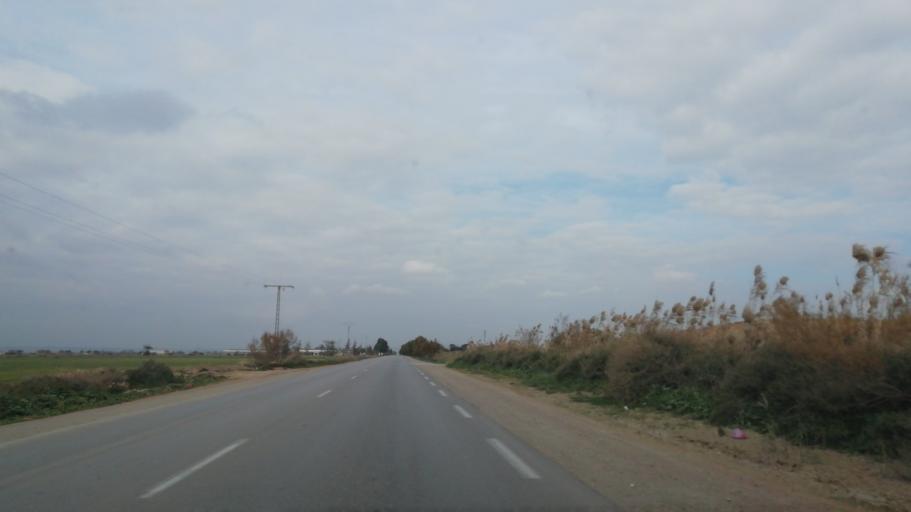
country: DZ
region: Mascara
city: Mascara
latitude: 35.6470
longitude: 0.0599
